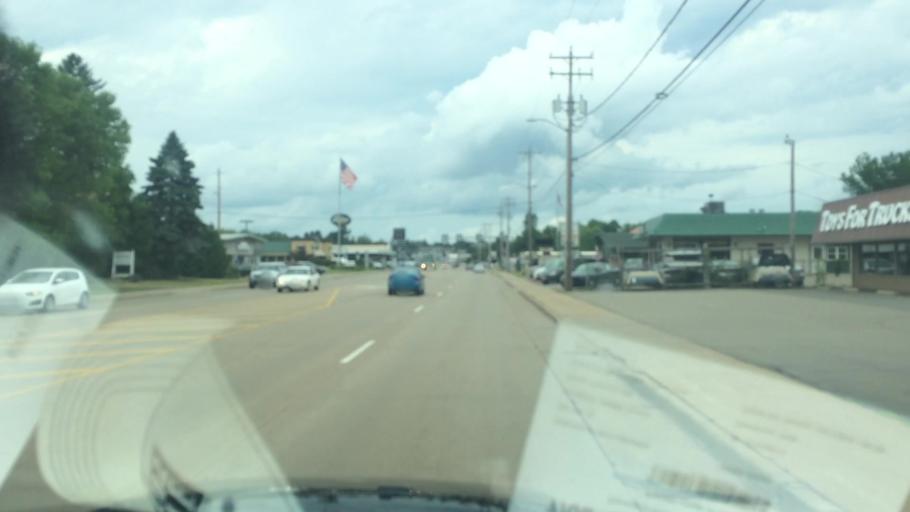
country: US
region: Wisconsin
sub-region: Marathon County
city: Schofield
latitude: 44.9238
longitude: -89.6132
